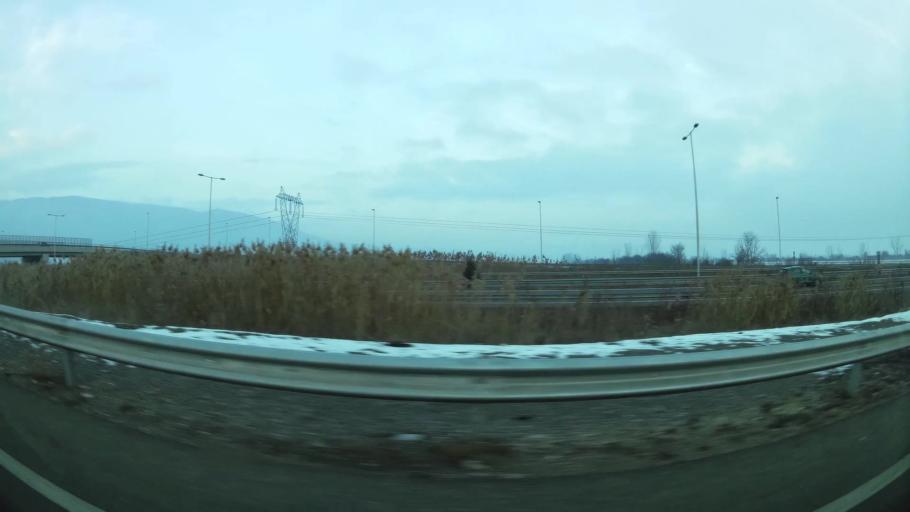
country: MK
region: Aracinovo
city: Arachinovo
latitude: 42.0174
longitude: 21.5336
